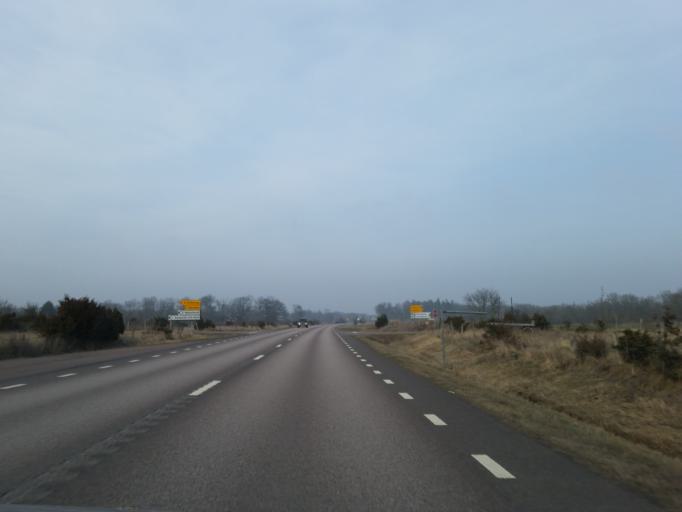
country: SE
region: Kalmar
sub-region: Borgholms Kommun
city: Borgholm
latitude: 57.1009
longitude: 16.9339
